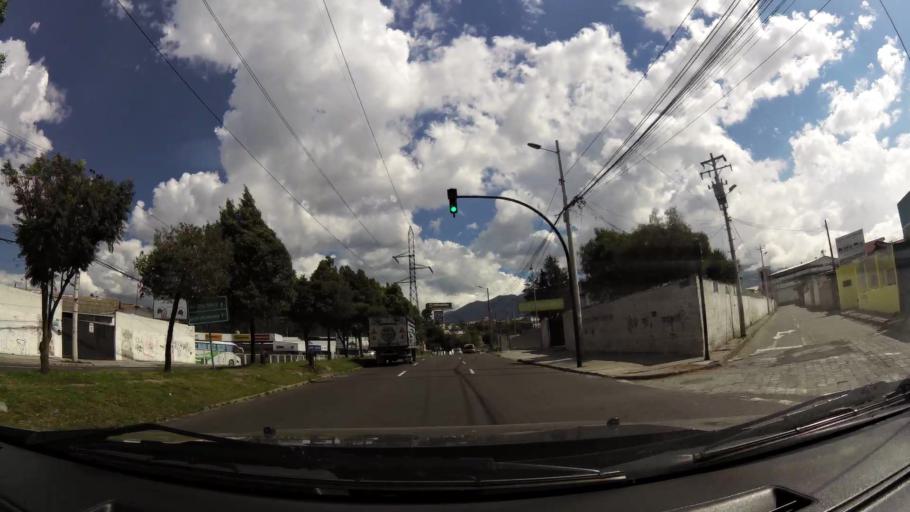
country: EC
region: Pichincha
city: Quito
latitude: -0.1040
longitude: -78.4704
